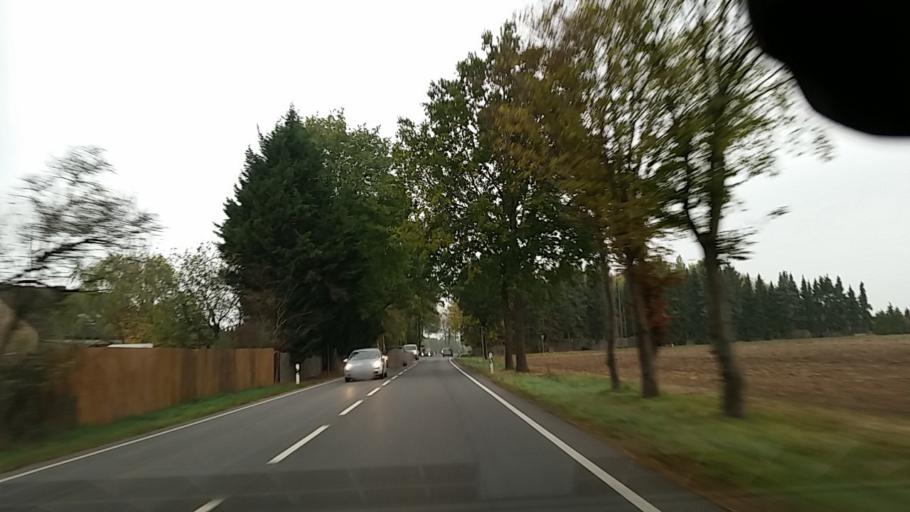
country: DE
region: Lower Saxony
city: Wrestedt
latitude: 52.9214
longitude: 10.6146
